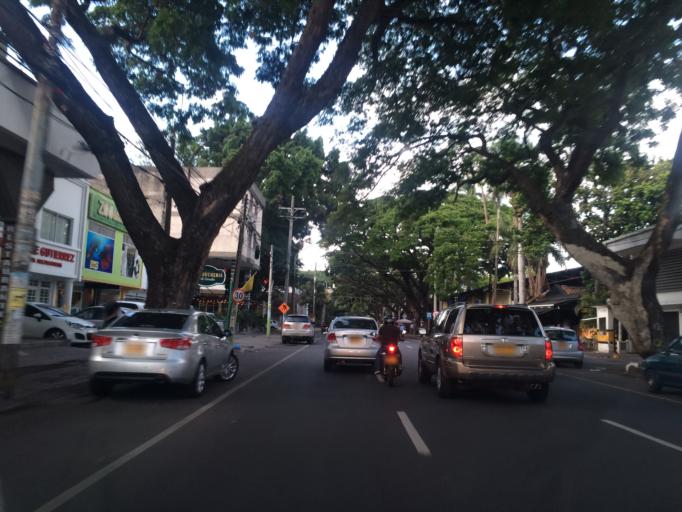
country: CO
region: Valle del Cauca
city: Cali
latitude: 3.4697
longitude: -76.5282
